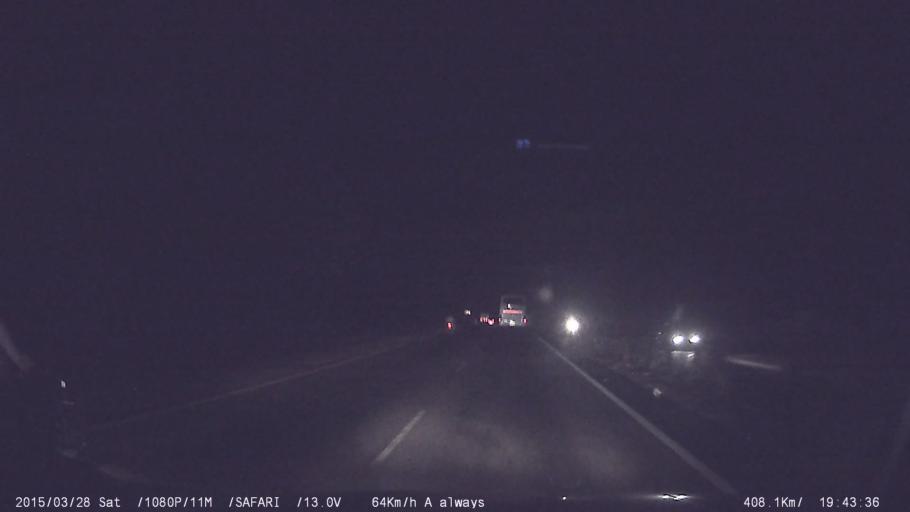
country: IN
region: Karnataka
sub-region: Mandya
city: Shrirangapattana
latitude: 12.4712
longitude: 76.7587
